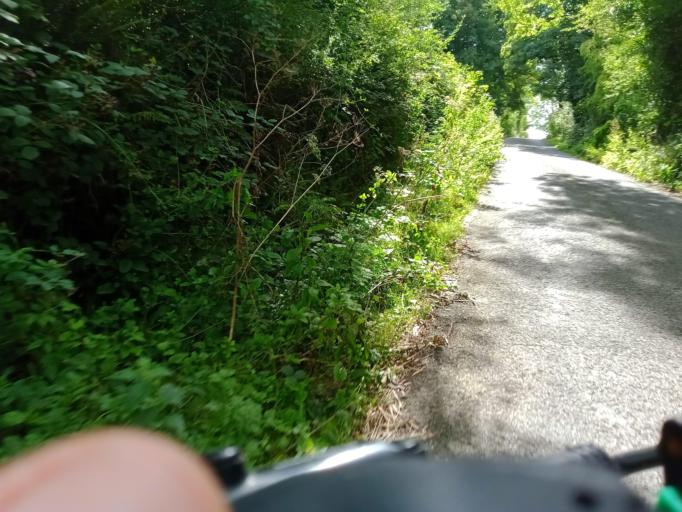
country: IE
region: Munster
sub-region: Waterford
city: Dungarvan
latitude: 52.1393
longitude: -7.5060
